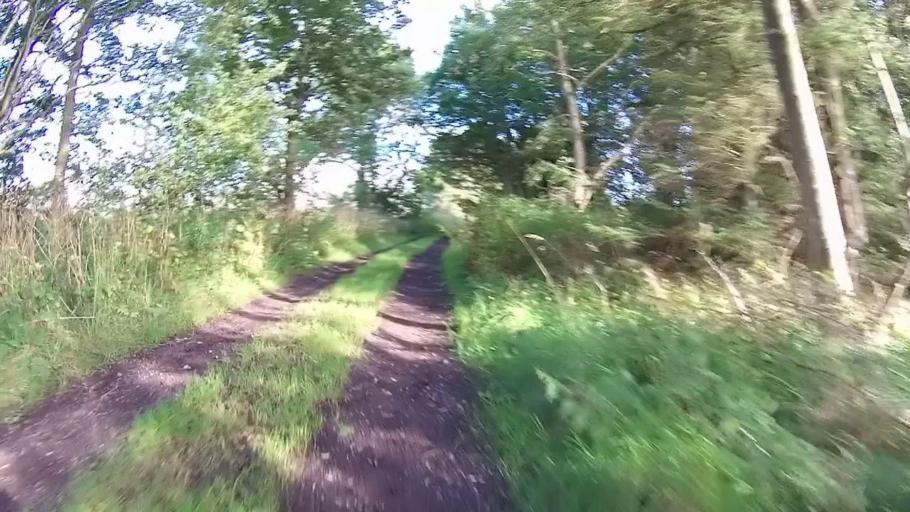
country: GB
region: Scotland
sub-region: Perth and Kinross
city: Milnathort
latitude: 56.2367
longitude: -3.3546
